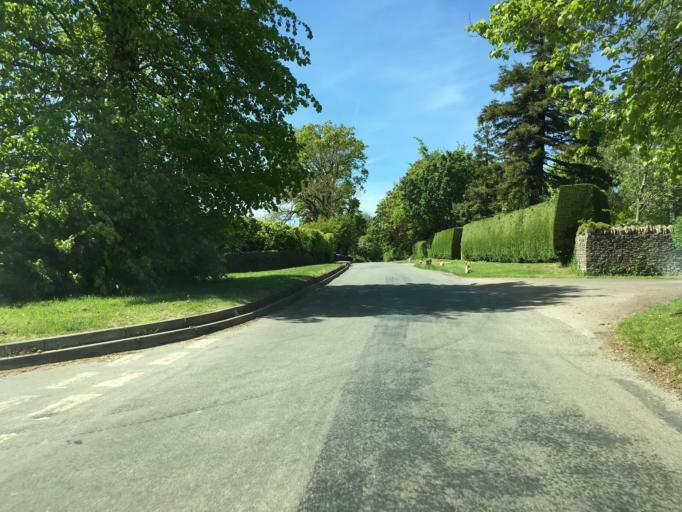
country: GB
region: England
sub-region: Gloucestershire
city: Coates
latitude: 51.7061
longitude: -2.0361
